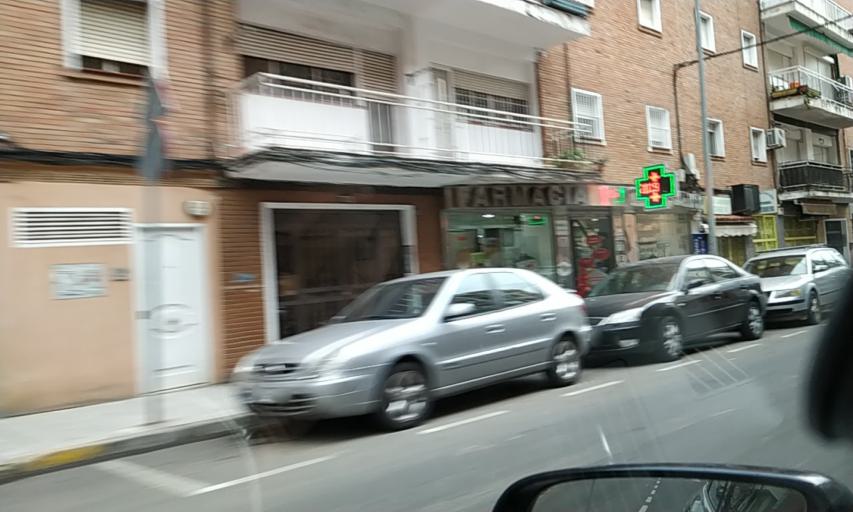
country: ES
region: Extremadura
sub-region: Provincia de Badajoz
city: Badajoz
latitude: 38.8884
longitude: -6.9767
